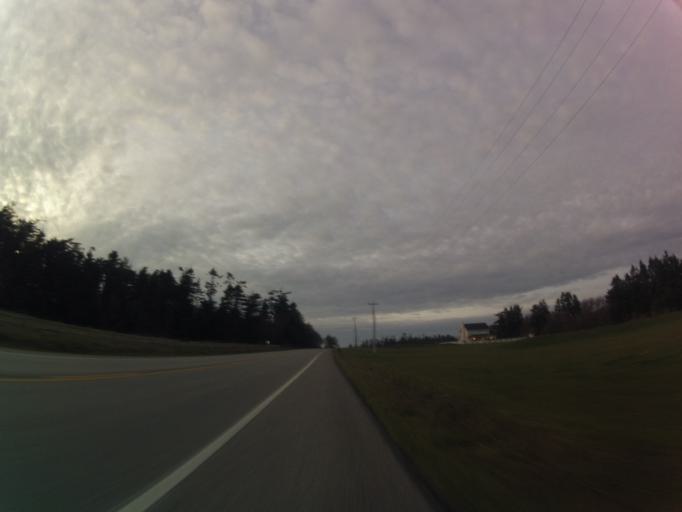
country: US
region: Washington
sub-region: Island County
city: Coupeville
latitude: 48.1737
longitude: -122.6818
